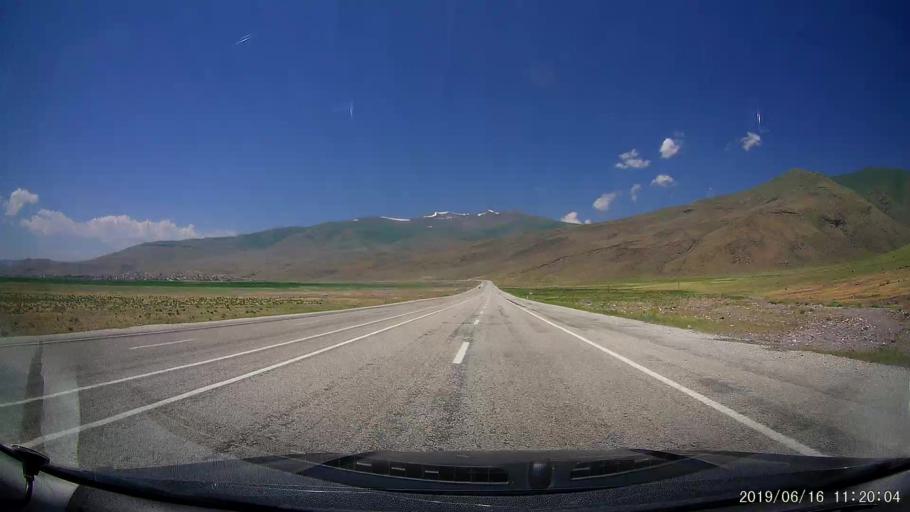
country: TR
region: Agri
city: Dogubayazit
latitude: 39.6968
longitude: 44.1000
